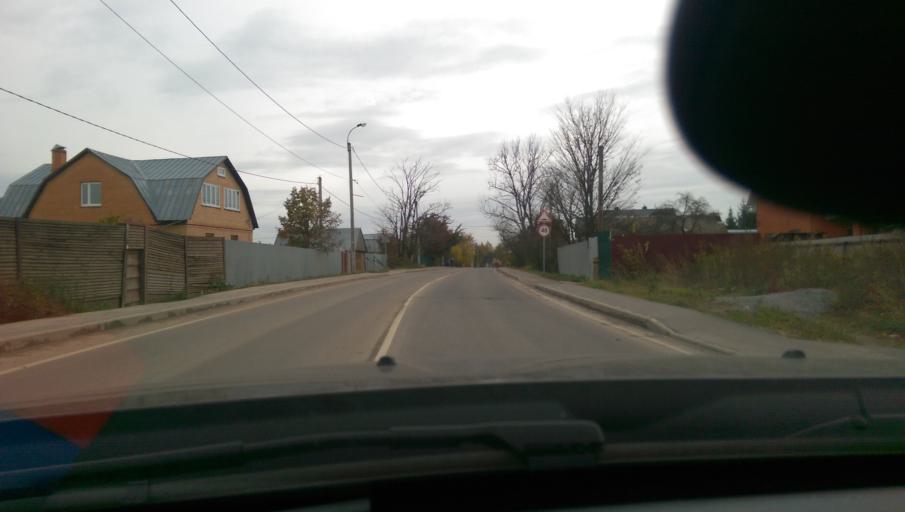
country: RU
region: Moskovskaya
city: Pirogovskiy
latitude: 56.0005
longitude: 37.7250
